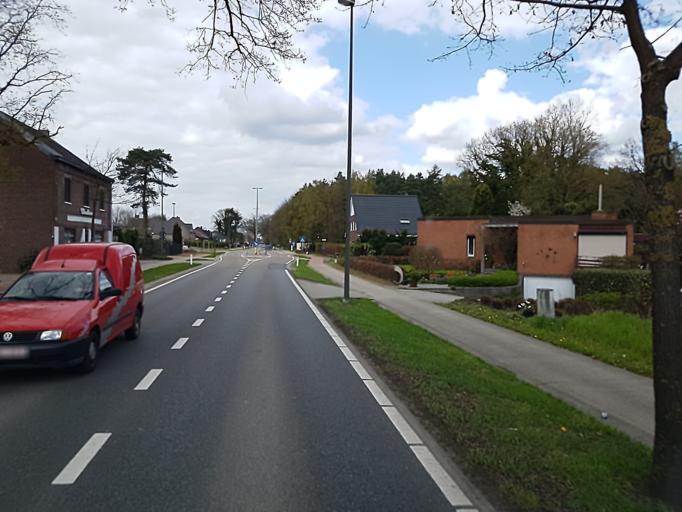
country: BE
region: Flanders
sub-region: Provincie Limburg
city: Zutendaal
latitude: 50.9426
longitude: 5.5593
